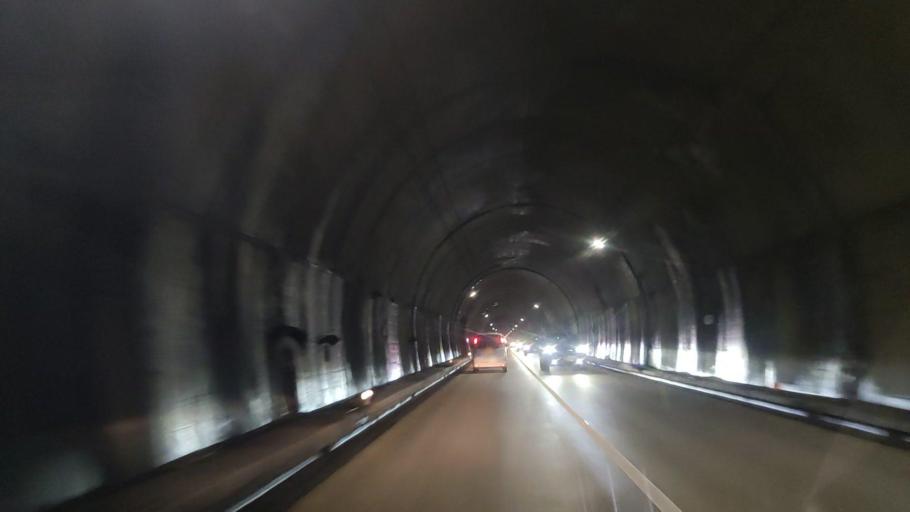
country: JP
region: Gifu
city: Takayama
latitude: 36.1815
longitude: 137.5228
